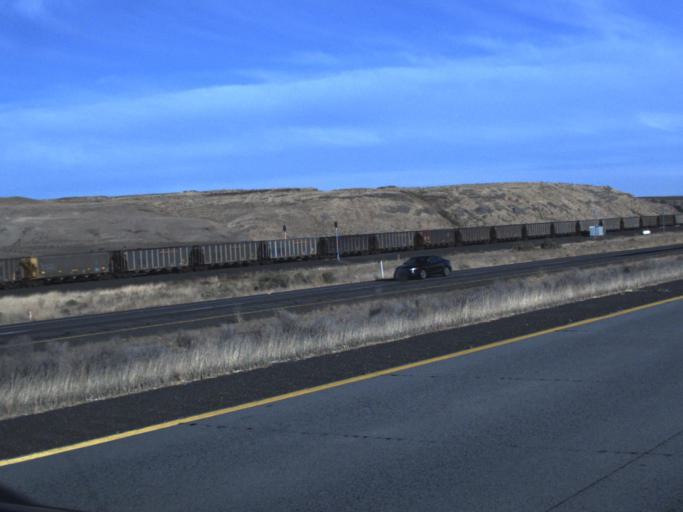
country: US
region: Washington
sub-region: Franklin County
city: Basin City
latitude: 46.4861
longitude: -119.0116
